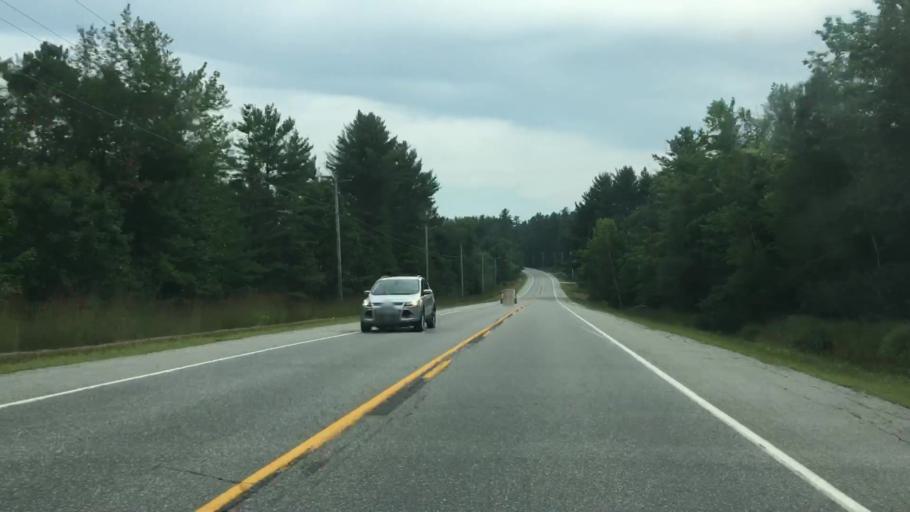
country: US
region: Maine
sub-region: Oxford County
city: Bethel
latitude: 44.4678
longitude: -70.7999
